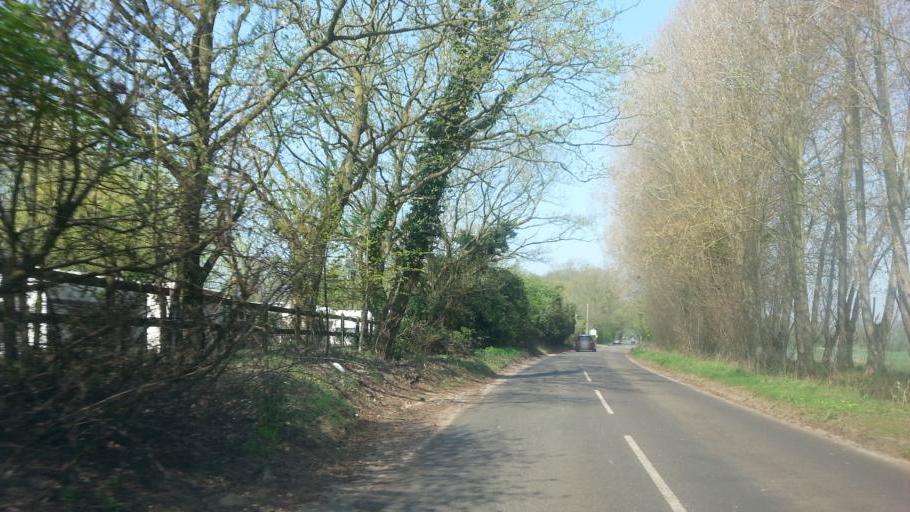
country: GB
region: England
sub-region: Suffolk
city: Thurston
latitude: 52.2400
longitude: 0.8257
